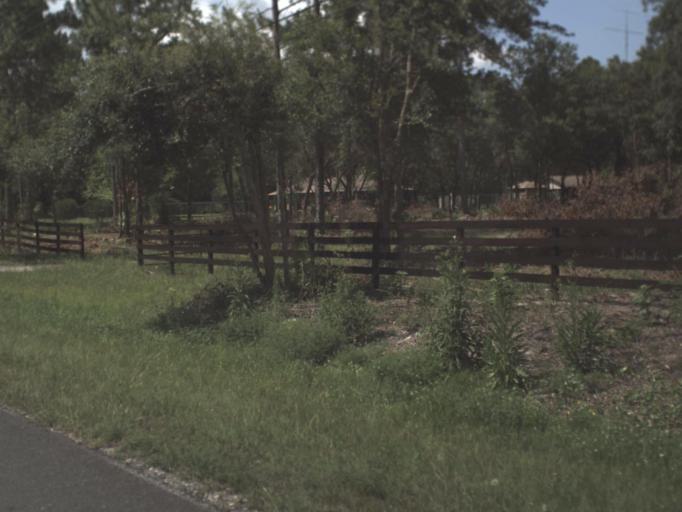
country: US
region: Florida
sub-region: Clay County
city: Green Cove Springs
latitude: 29.9731
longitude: -81.5399
